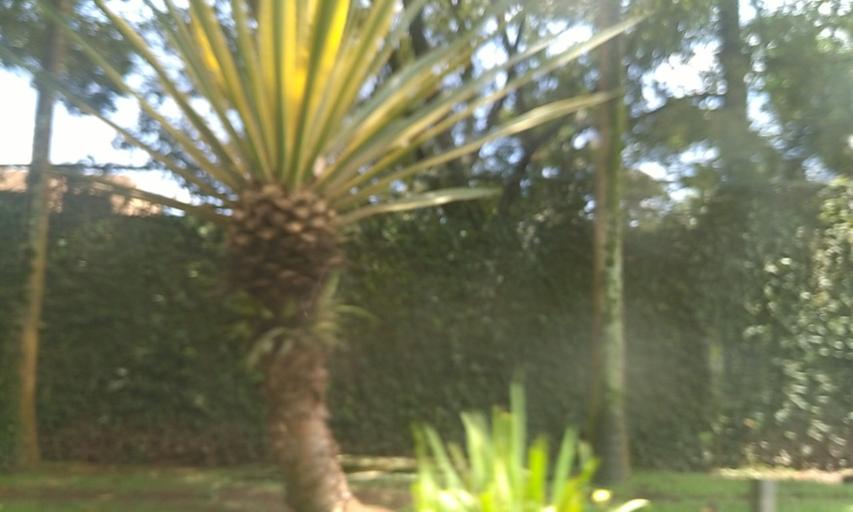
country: UG
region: Central Region
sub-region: Kampala District
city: Kampala
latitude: 0.3352
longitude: 32.5968
